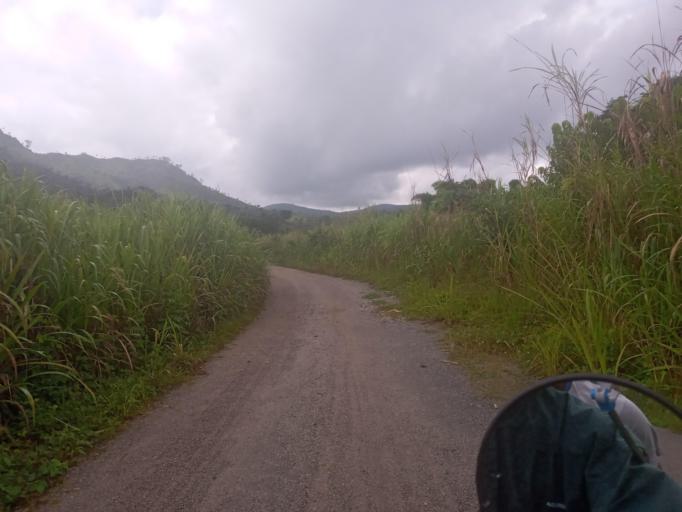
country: SL
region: Northern Province
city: Bumbuna
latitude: 8.9288
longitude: -11.7474
